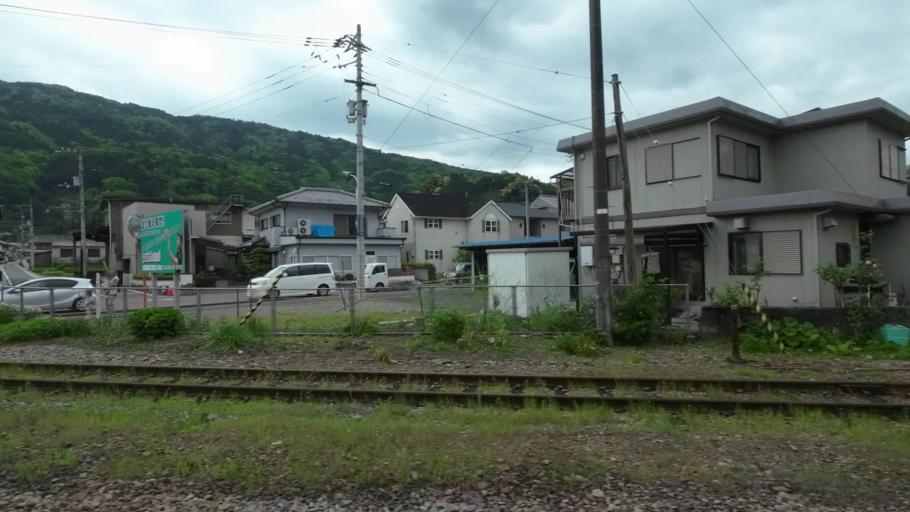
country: JP
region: Tokushima
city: Ikedacho
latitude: 34.0282
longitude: 133.8027
